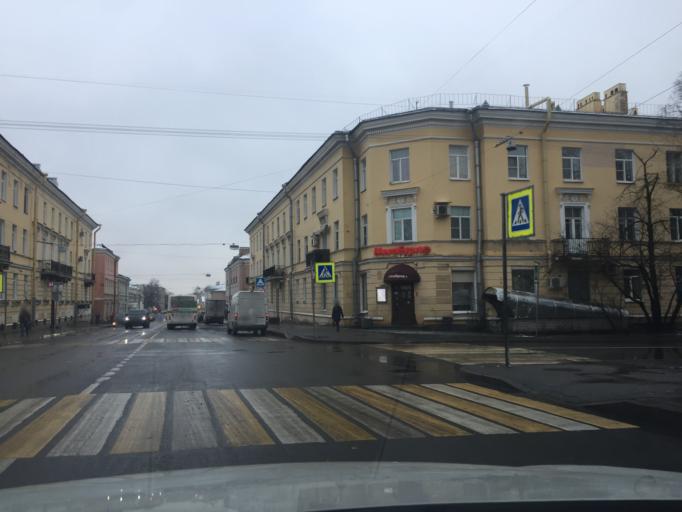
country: RU
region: St.-Petersburg
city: Pushkin
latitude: 59.7175
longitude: 30.4060
